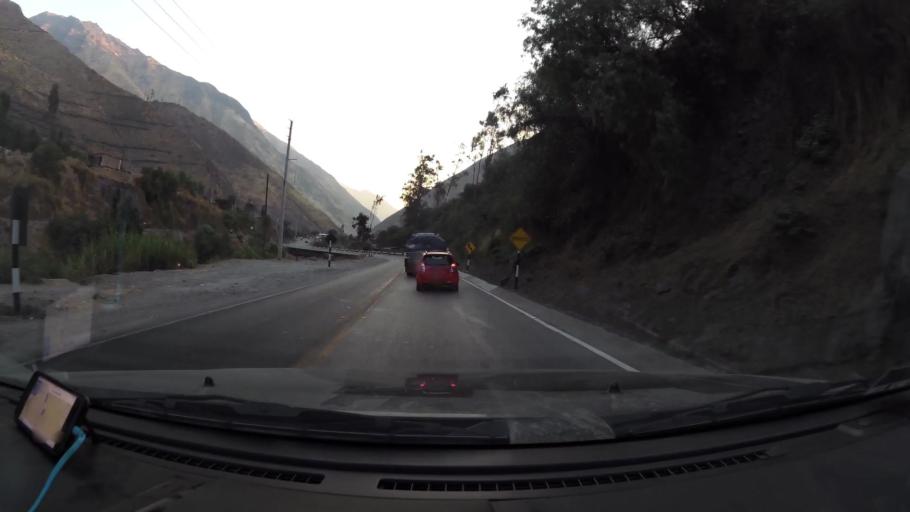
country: PE
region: Lima
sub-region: Provincia de Huarochiri
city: Matucana
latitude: -11.8394
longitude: -76.3784
